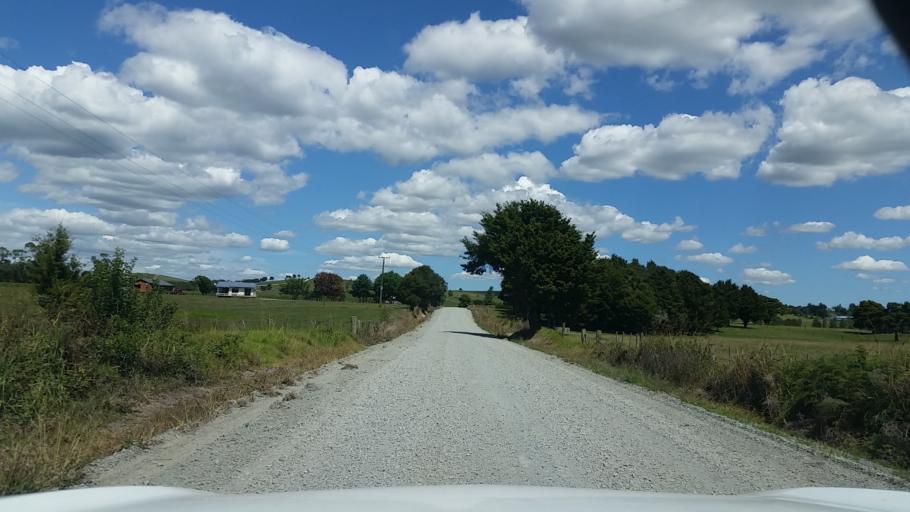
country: NZ
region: Northland
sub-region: Whangarei
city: Maungatapere
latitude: -35.6986
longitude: 174.1452
